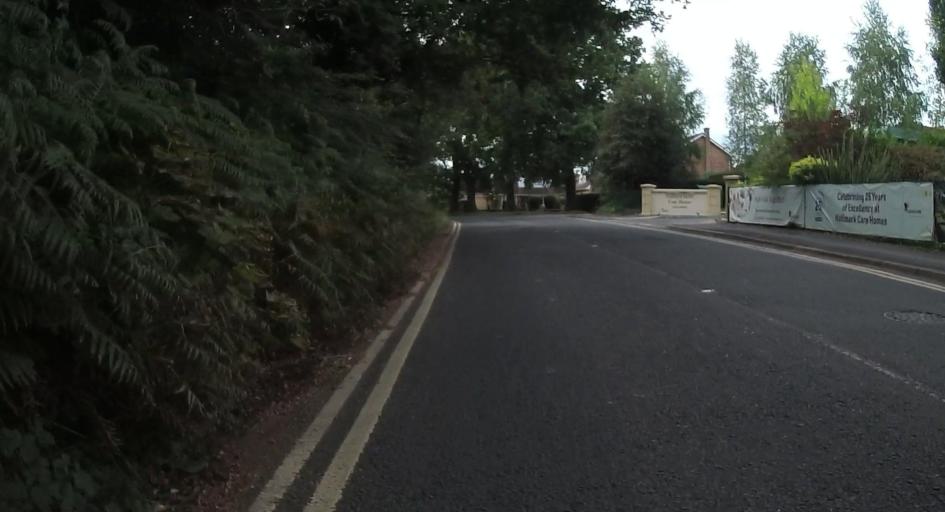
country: GB
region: England
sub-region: Surrey
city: Windlesham
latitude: 51.3489
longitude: -0.6636
